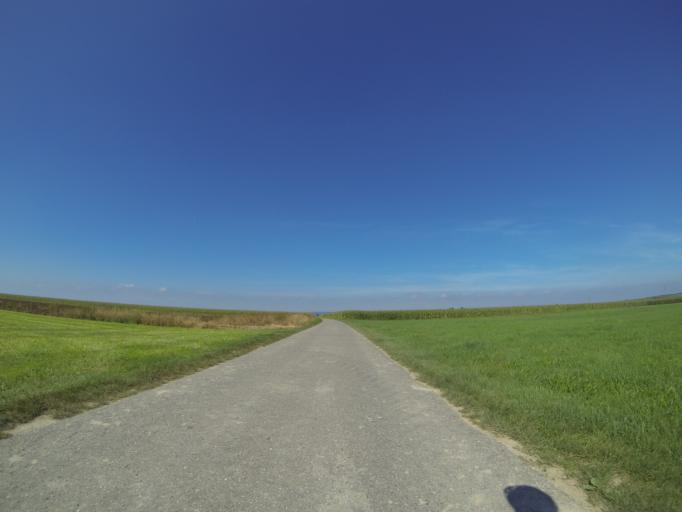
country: DE
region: Baden-Wuerttemberg
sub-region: Tuebingen Region
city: Achstetten
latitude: 48.2686
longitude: 9.9183
